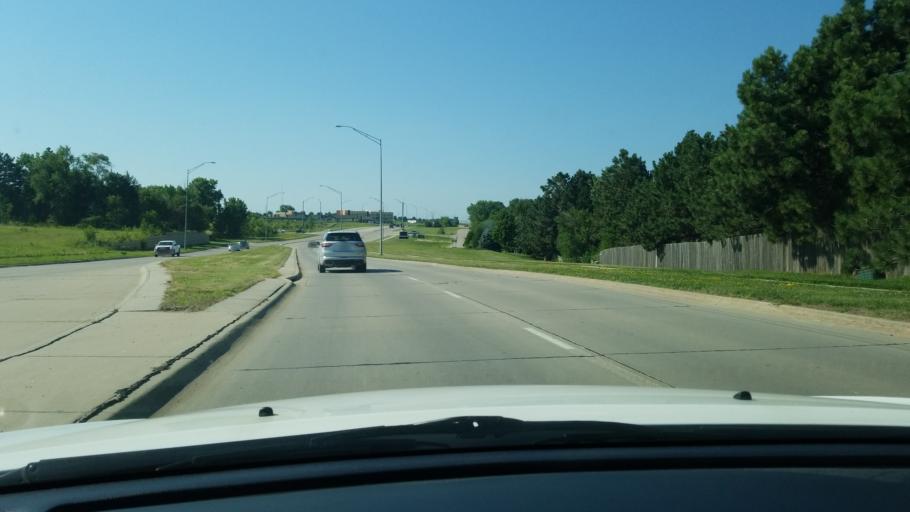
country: US
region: Nebraska
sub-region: Lancaster County
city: Lincoln
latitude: 40.7443
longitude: -96.6061
